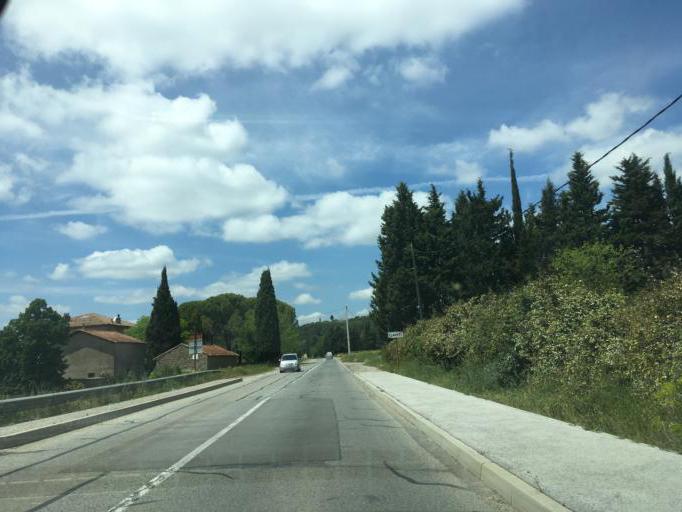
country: FR
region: Provence-Alpes-Cote d'Azur
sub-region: Departement du Var
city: Flayosc
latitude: 43.5396
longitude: 6.3795
